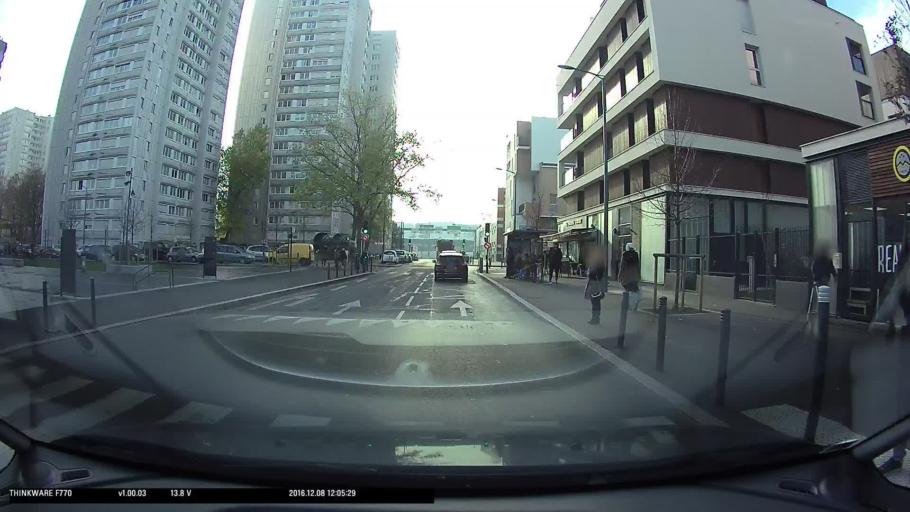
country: FR
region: Ile-de-France
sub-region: Departement de Seine-Saint-Denis
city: Bobigny
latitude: 48.9058
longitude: 2.4443
